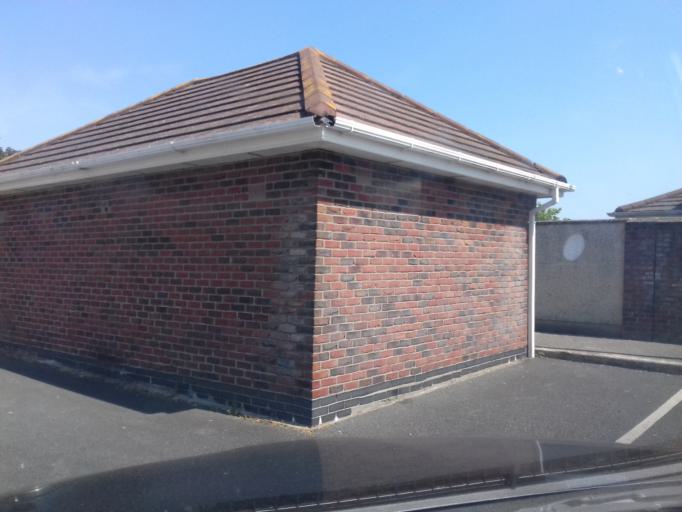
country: IE
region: Leinster
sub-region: Fingal County
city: Baldoyle
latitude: 53.3952
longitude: -6.1286
